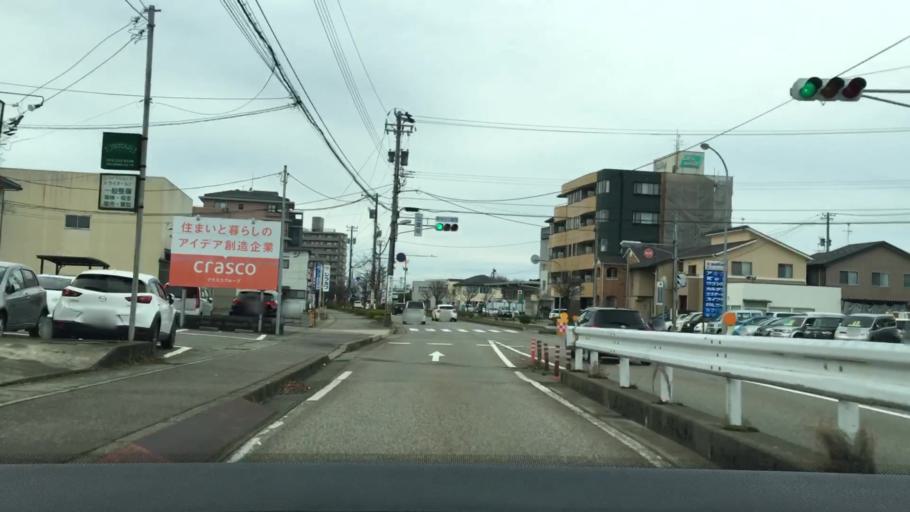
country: JP
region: Ishikawa
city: Kanazawa-shi
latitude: 36.5756
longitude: 136.6248
